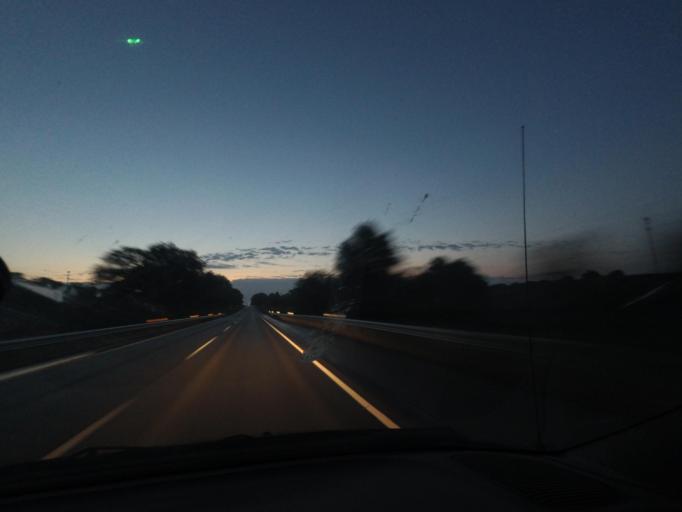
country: US
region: Missouri
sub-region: Linn County
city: Linneus
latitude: 39.7774
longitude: -93.3126
